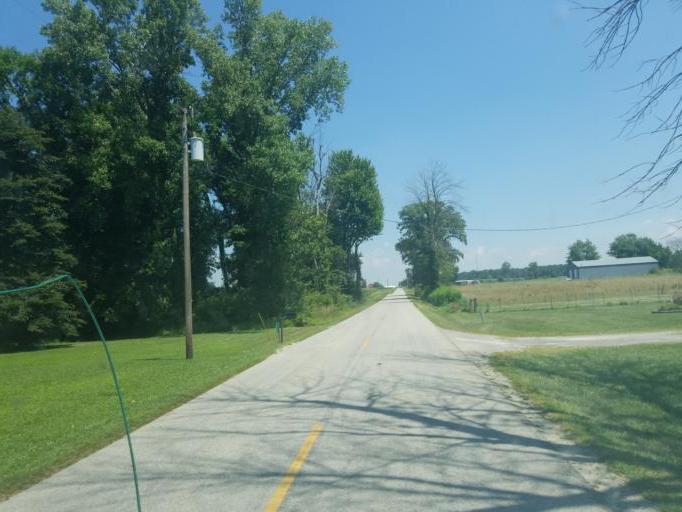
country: US
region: Ohio
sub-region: Shelby County
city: Botkins
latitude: 40.4823
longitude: -84.1940
